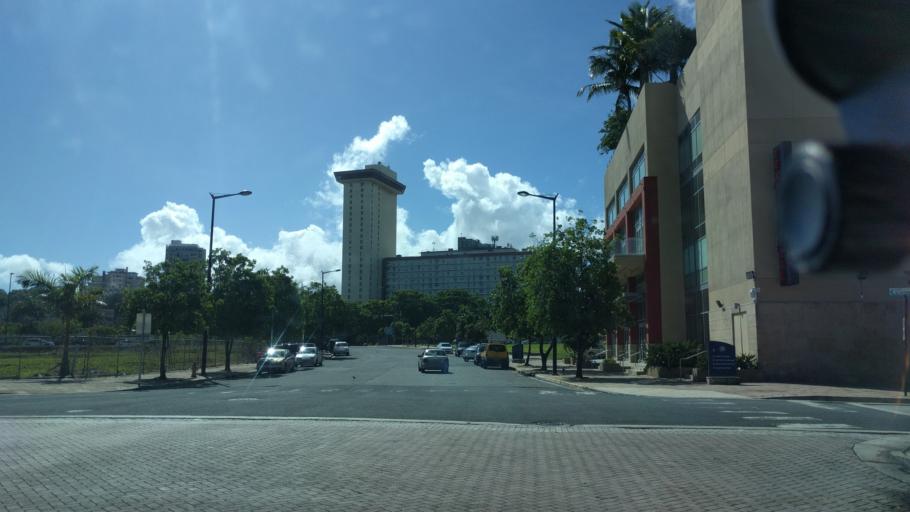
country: PR
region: San Juan
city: San Juan
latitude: 18.4555
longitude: -66.0904
